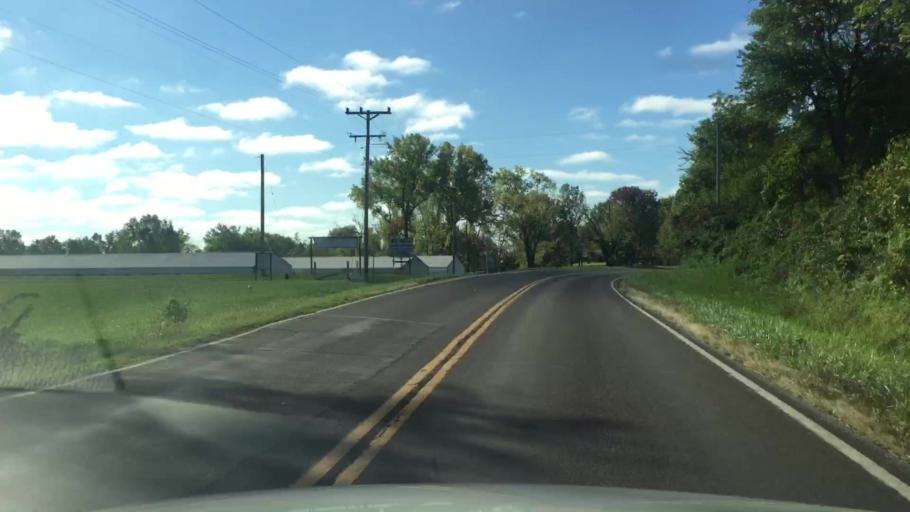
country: US
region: Missouri
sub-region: Howard County
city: New Franklin
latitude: 39.0348
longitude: -92.7434
